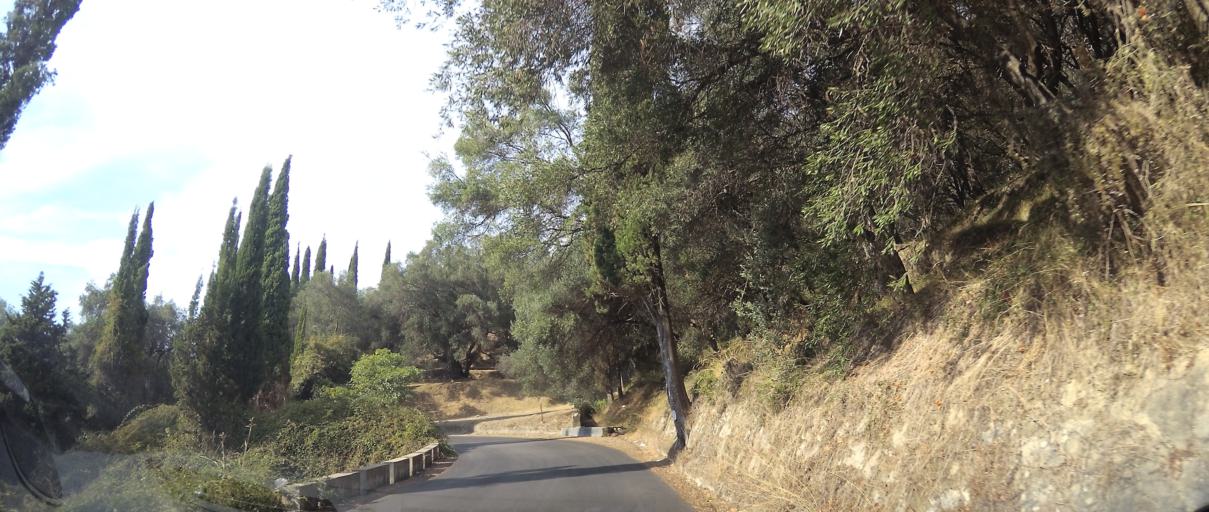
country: GR
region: Ionian Islands
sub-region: Nomos Kerkyras
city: Kynopiastes
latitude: 39.5470
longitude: 19.8681
